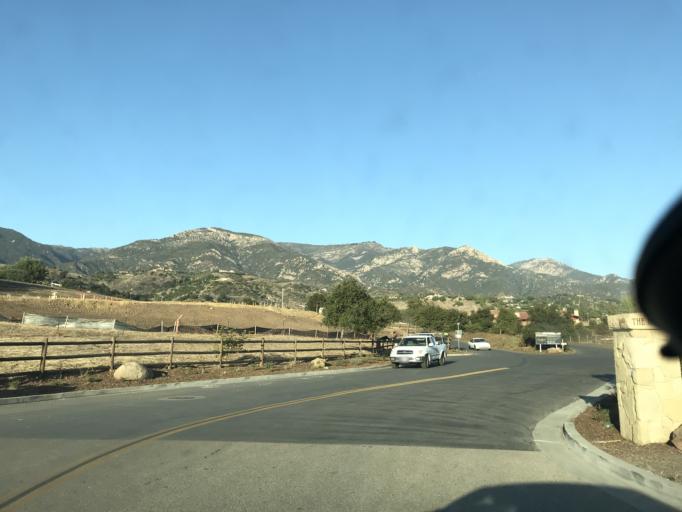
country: US
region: California
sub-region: Santa Barbara County
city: Mission Canyon
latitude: 34.4565
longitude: -119.7594
